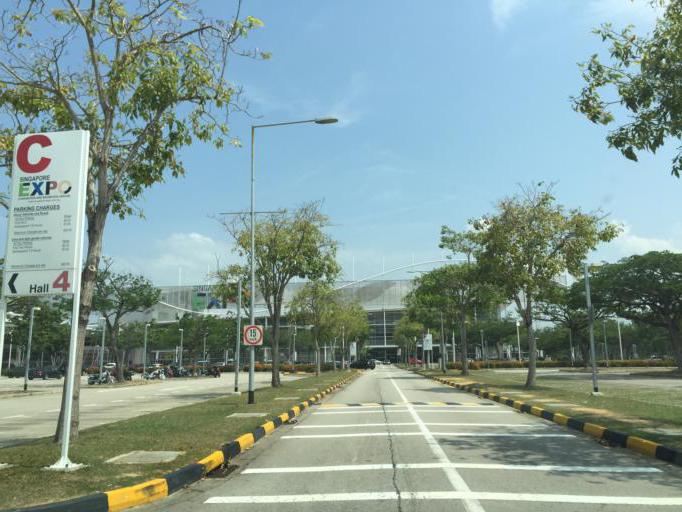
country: SG
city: Singapore
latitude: 1.3350
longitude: 103.9590
